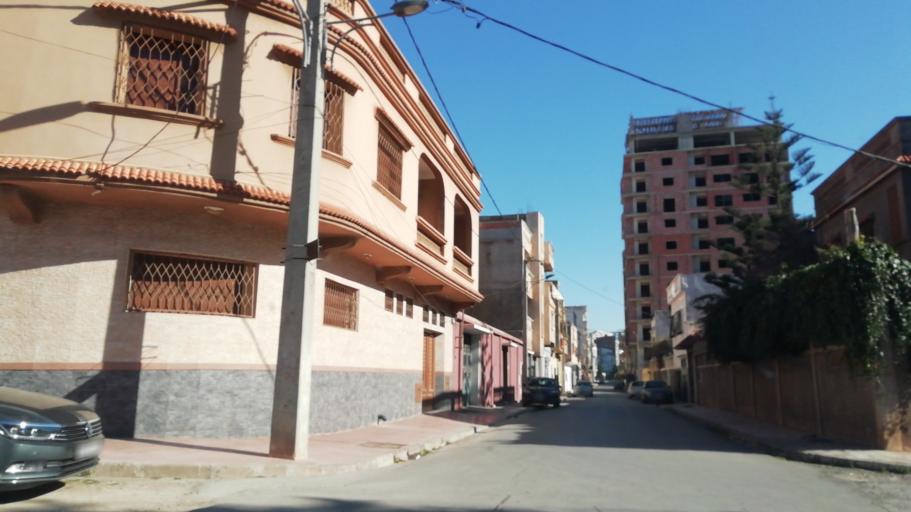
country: DZ
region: Oran
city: Oran
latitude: 35.7137
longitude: -0.6192
